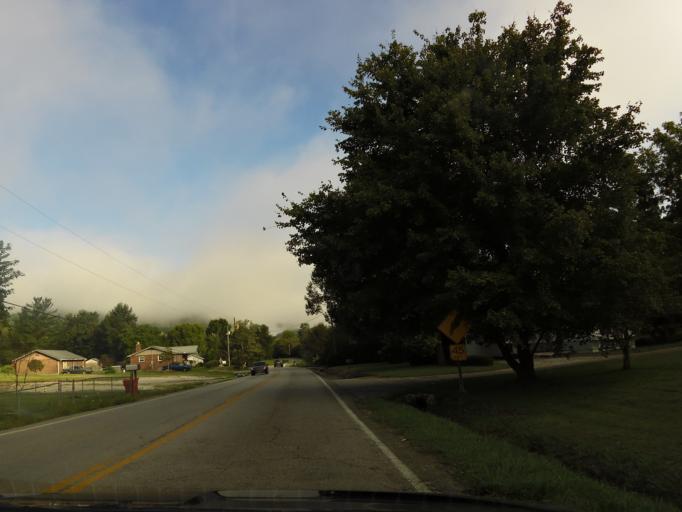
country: US
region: Kentucky
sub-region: Whitley County
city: Williamsburg
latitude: 36.7055
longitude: -84.1470
